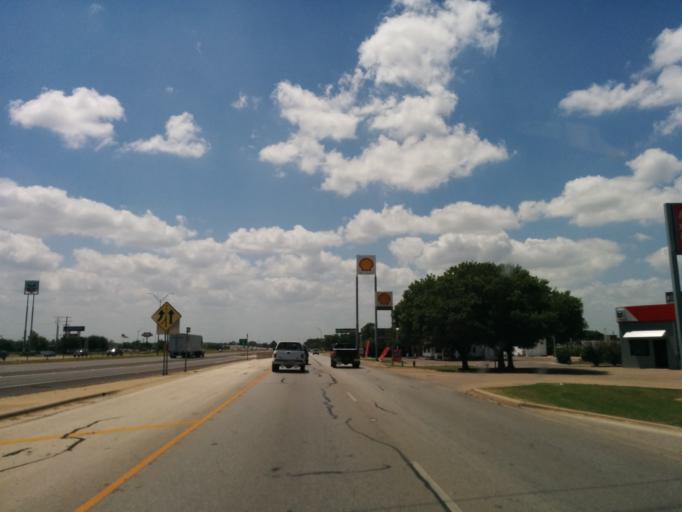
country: US
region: Texas
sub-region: Bastrop County
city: Bastrop
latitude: 30.1086
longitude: -97.3378
